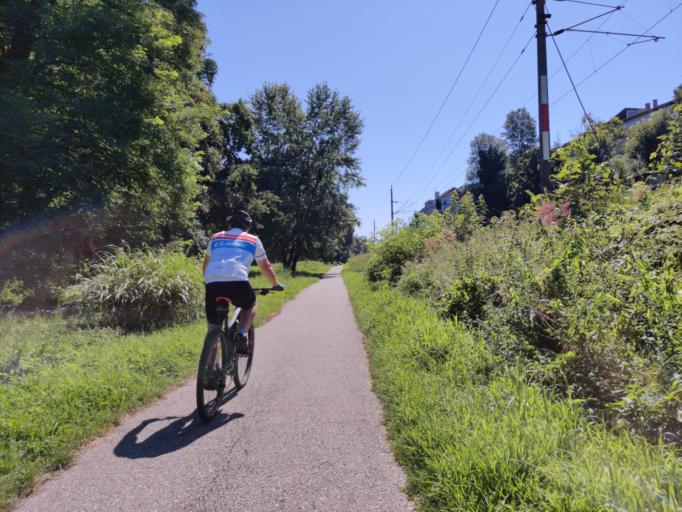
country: AT
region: Styria
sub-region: Politischer Bezirk Leibnitz
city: Wildon
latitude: 46.8882
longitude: 15.5121
